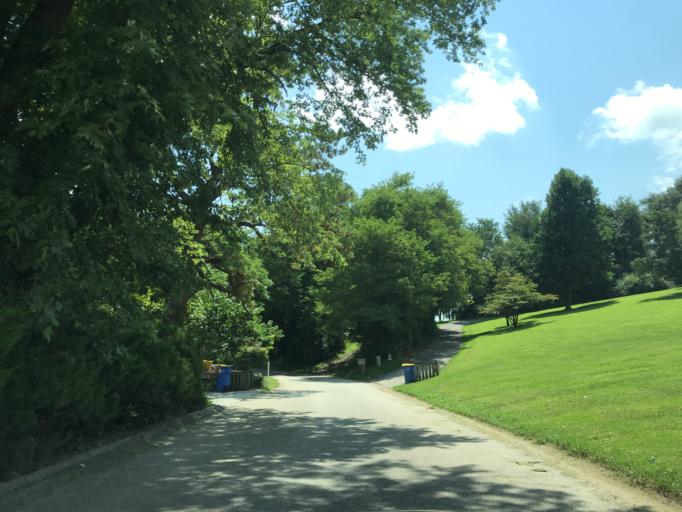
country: US
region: Pennsylvania
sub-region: York County
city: New Freedom
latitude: 39.7228
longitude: -76.7193
